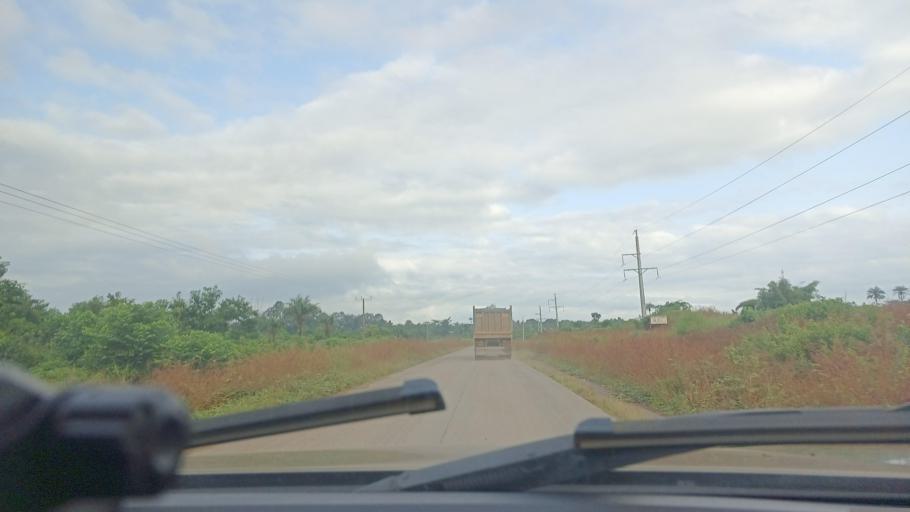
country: LR
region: Montserrado
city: Monrovia
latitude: 6.5772
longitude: -10.8858
